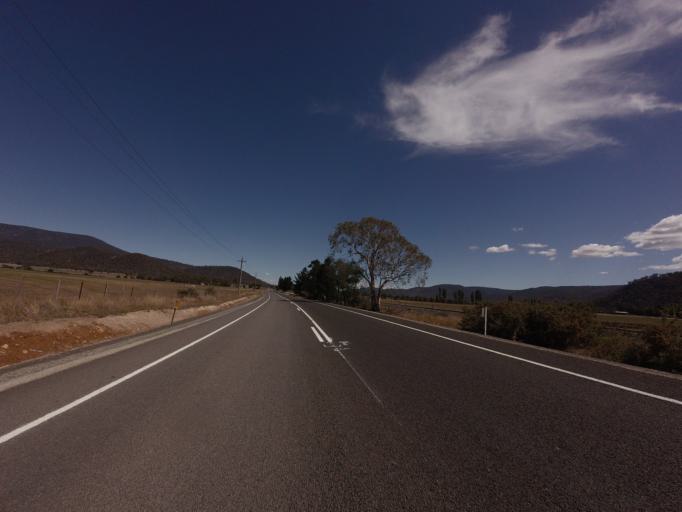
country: AU
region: Tasmania
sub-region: Break O'Day
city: St Helens
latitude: -41.6667
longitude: 147.9066
